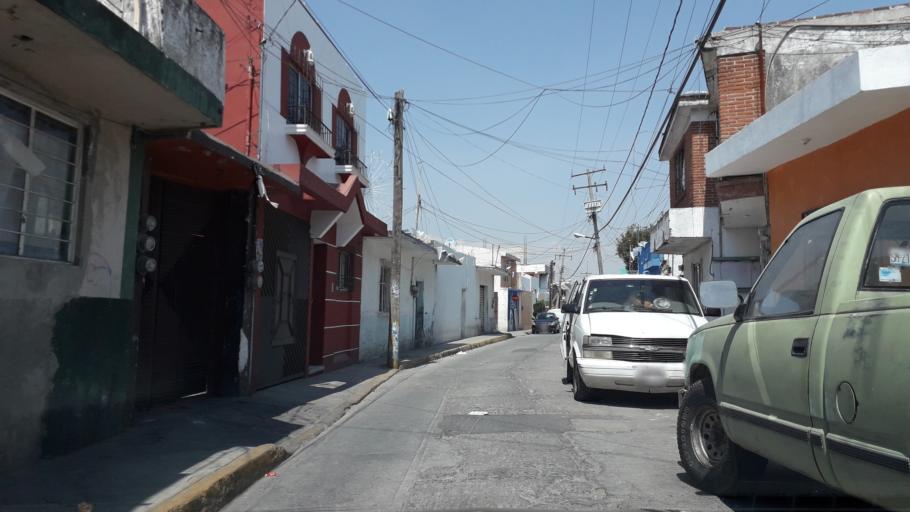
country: MX
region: Puebla
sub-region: Cuautlancingo
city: Sanctorum
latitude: 19.0911
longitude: -98.2189
